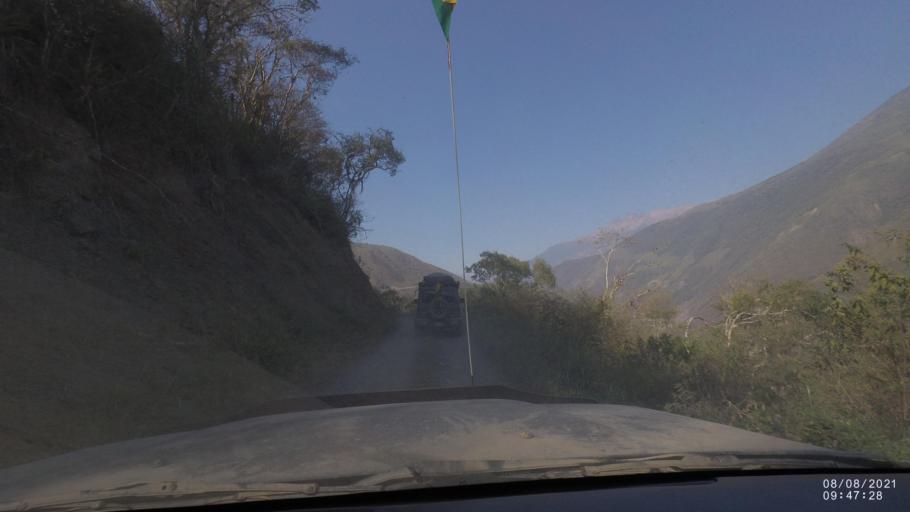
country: BO
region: La Paz
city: Quime
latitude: -16.6093
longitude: -66.7295
